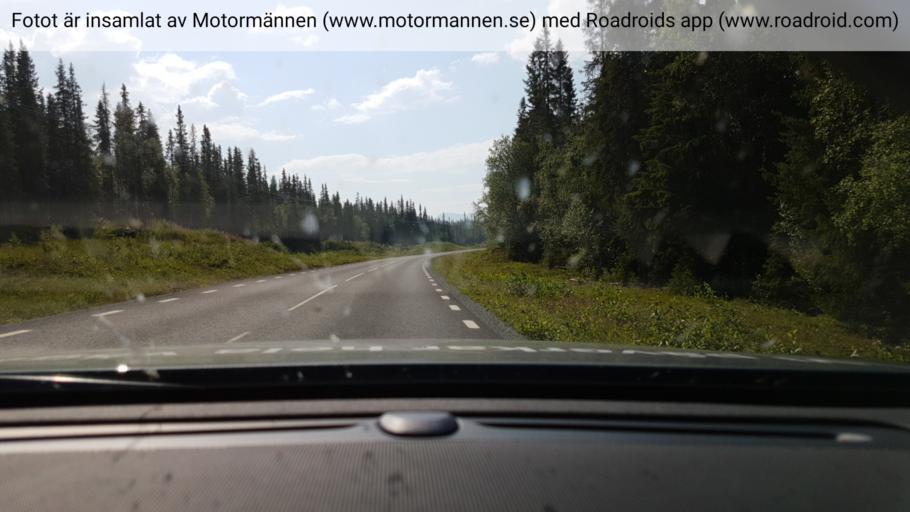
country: SE
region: Vaesterbotten
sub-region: Vilhelmina Kommun
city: Sjoberg
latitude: 65.6171
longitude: 15.5349
